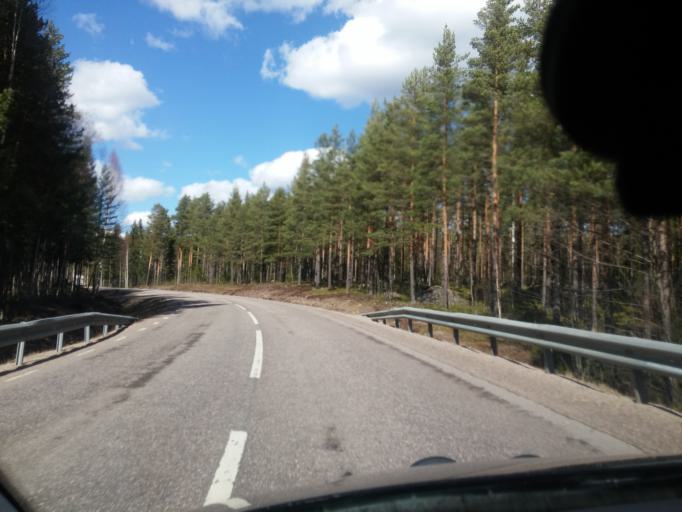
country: SE
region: Gaevleborg
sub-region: Ovanakers Kommun
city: Edsbyn
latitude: 61.2502
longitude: 15.8934
